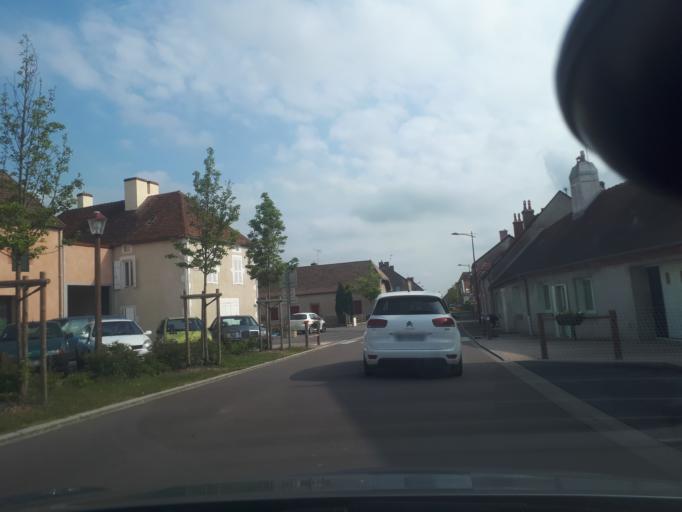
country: FR
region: Auvergne
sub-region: Departement de l'Allier
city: Dompierre-sur-Besbre
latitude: 46.4465
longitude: 3.6304
